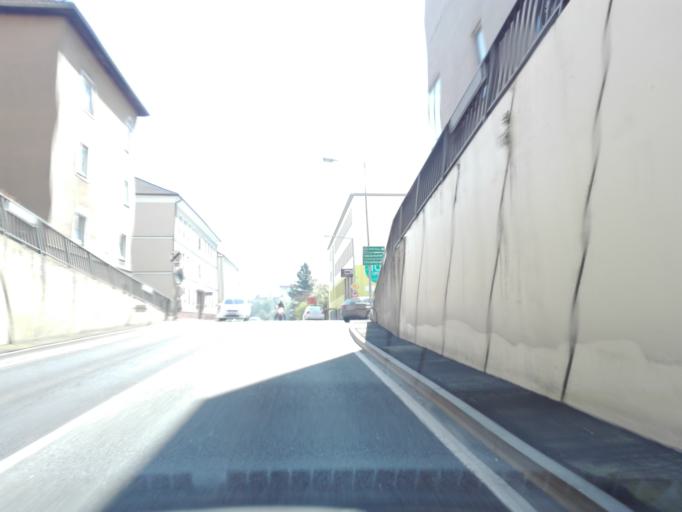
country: AT
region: Upper Austria
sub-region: Steyr Stadt
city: Steyr
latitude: 48.0381
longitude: 14.4110
